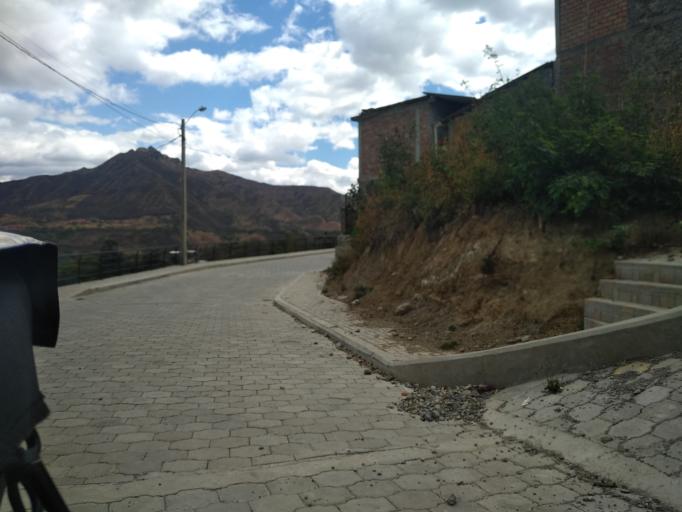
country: EC
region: Loja
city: Loja
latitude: -4.2439
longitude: -79.2211
